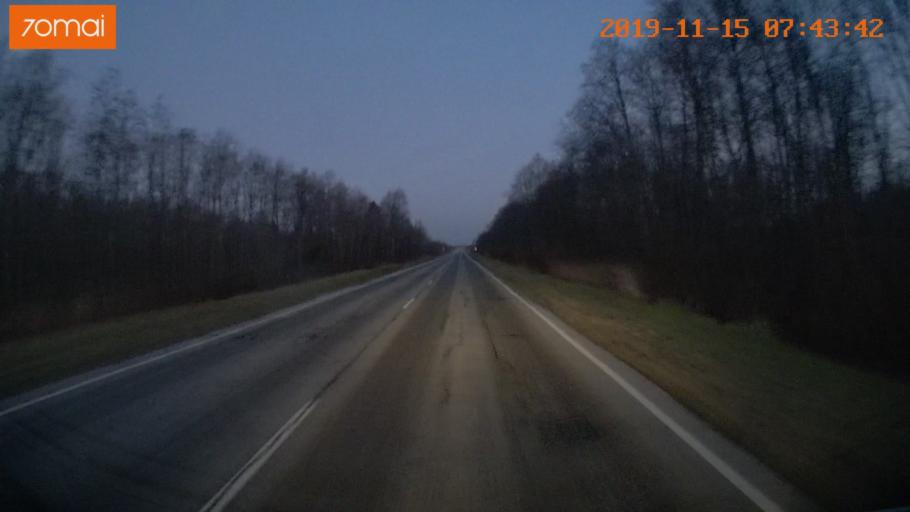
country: RU
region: Vologda
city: Sheksna
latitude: 58.8054
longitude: 38.3240
